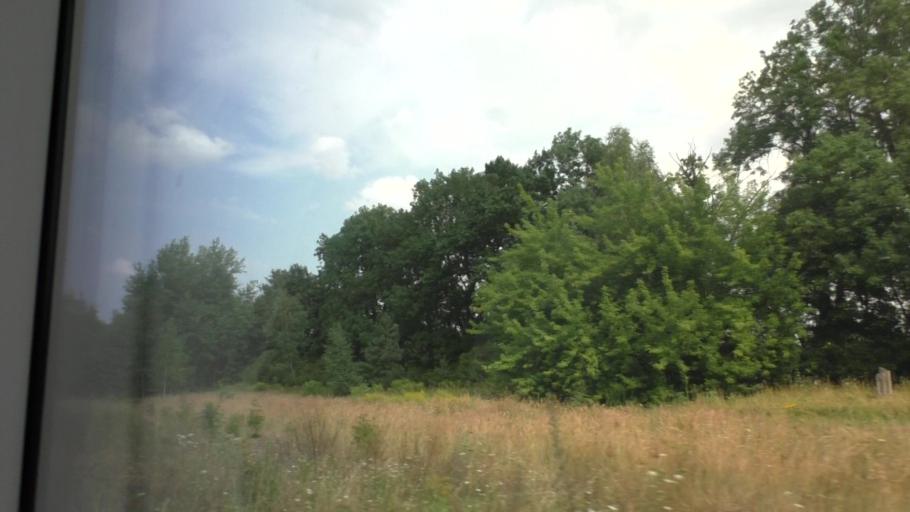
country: DE
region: Brandenburg
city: Mixdorf
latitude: 52.1671
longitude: 14.3793
